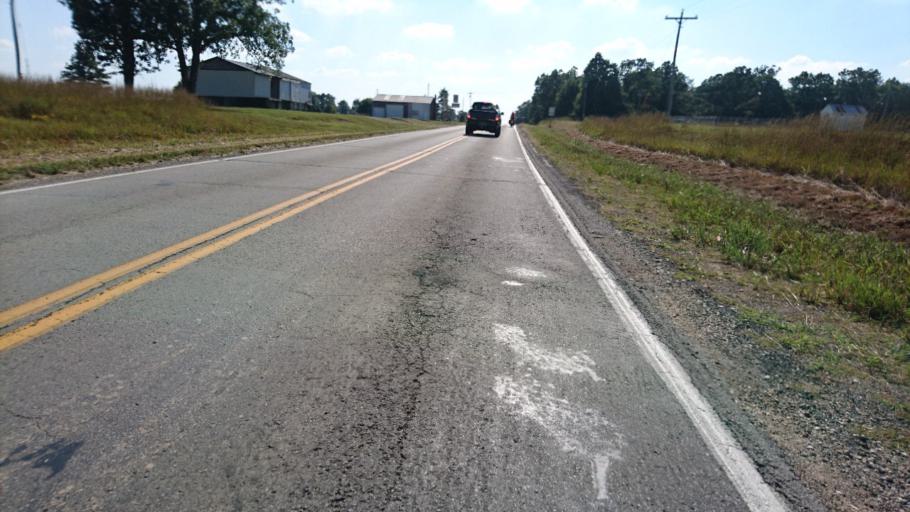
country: US
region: Missouri
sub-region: Laclede County
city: Lebanon
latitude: 37.6396
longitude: -92.6763
